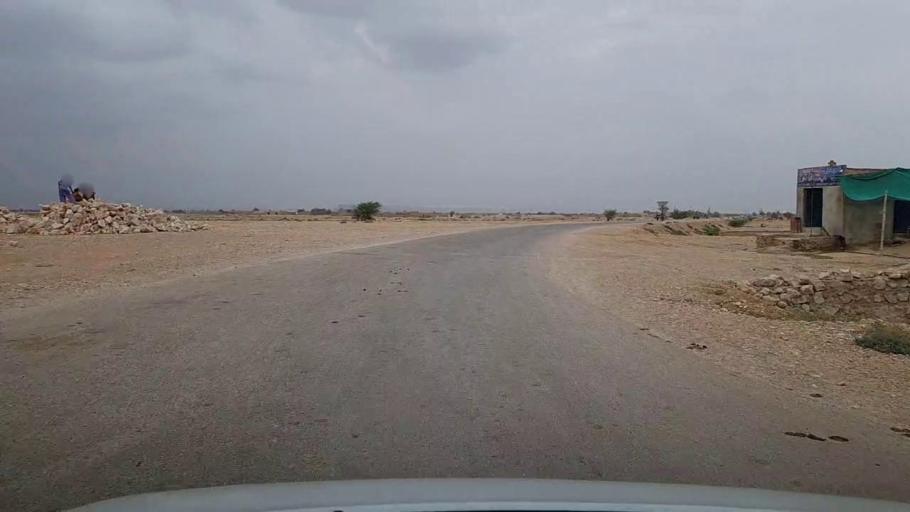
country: PK
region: Sindh
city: Sehwan
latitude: 26.3340
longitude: 67.7235
